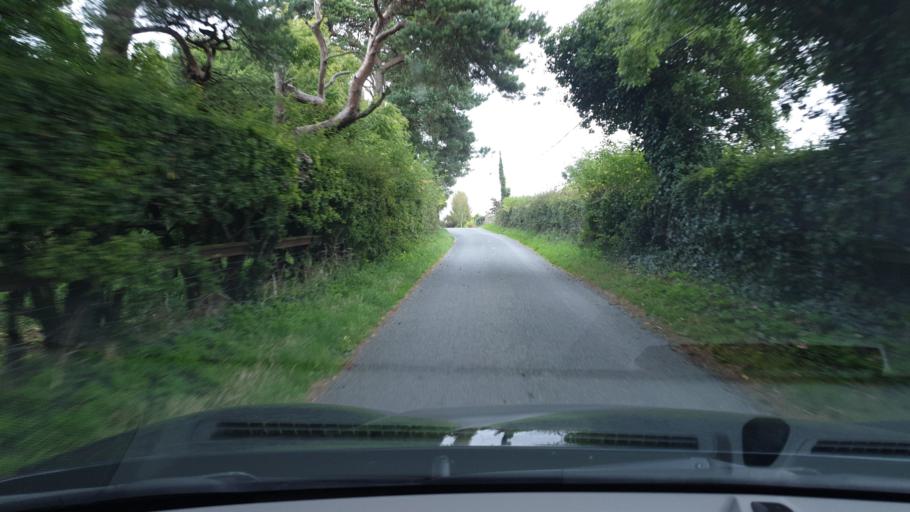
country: IE
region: Leinster
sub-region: An Mhi
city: Dunshaughlin
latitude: 53.4920
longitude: -6.5641
